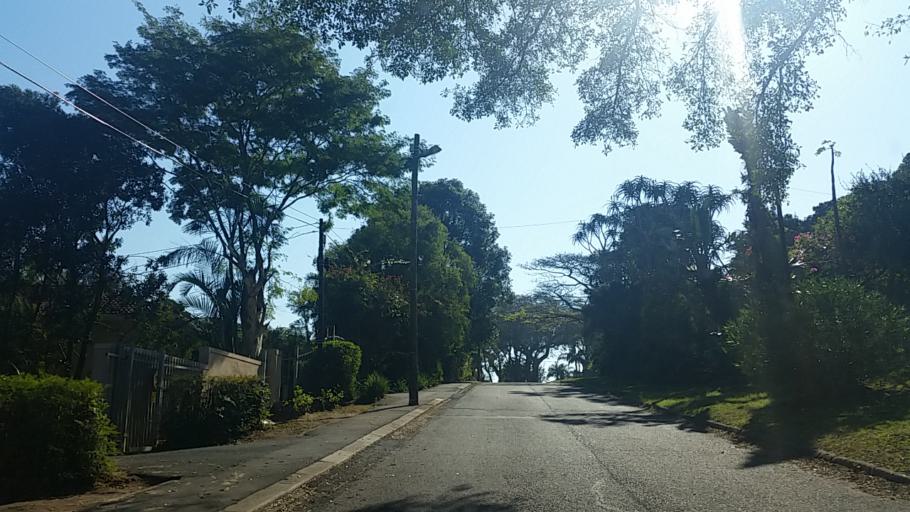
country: ZA
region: KwaZulu-Natal
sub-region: eThekwini Metropolitan Municipality
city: Berea
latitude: -29.8402
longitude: 30.9045
